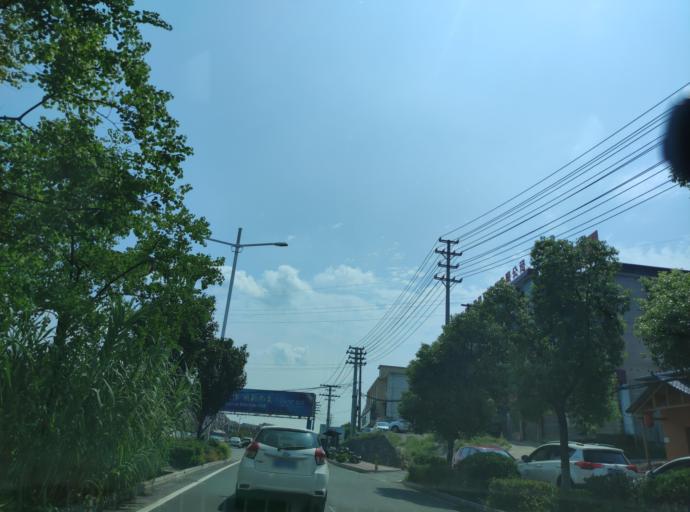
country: CN
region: Jiangxi Sheng
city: Pingxiang
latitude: 27.6590
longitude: 113.8973
